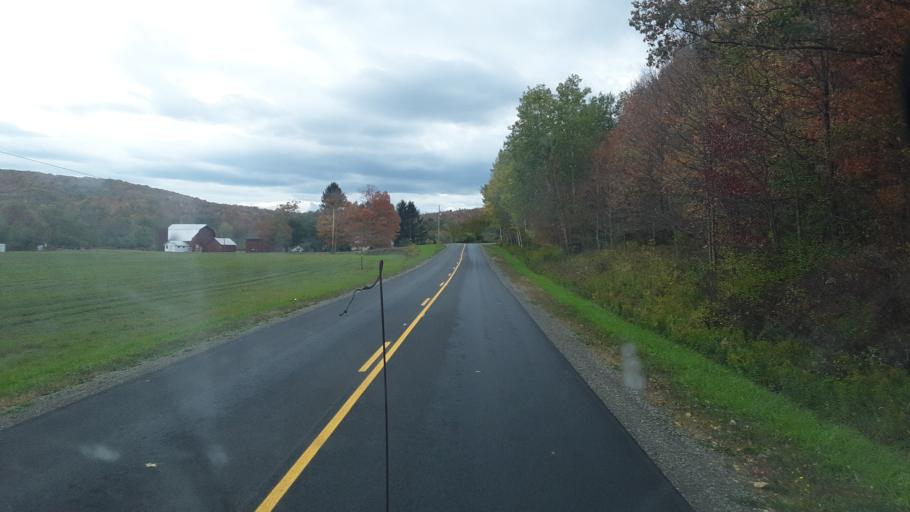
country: US
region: New York
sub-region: Allegany County
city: Alfred
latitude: 42.3659
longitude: -77.8181
